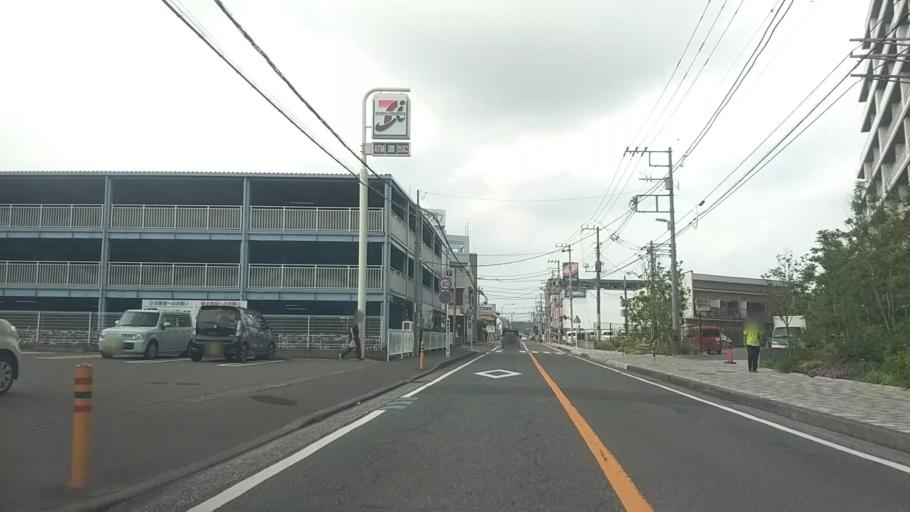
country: JP
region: Kanagawa
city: Fujisawa
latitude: 35.3382
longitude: 139.4416
